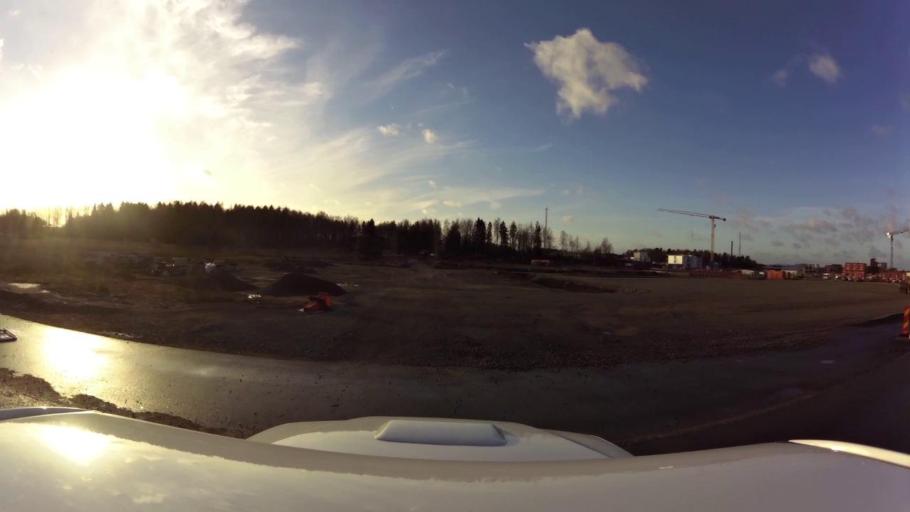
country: SE
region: OEstergoetland
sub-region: Linkopings Kommun
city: Linkoping
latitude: 58.3930
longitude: 15.5884
